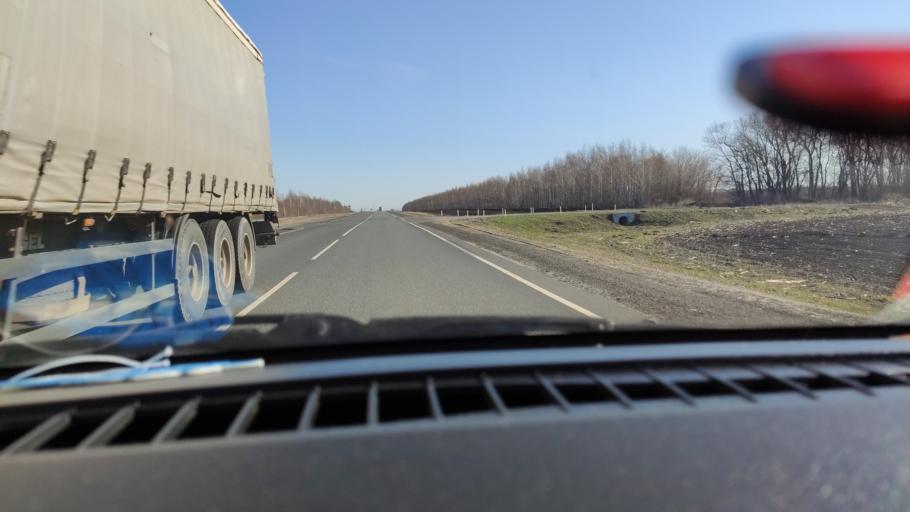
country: RU
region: Samara
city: Syzran'
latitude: 52.9867
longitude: 48.3180
